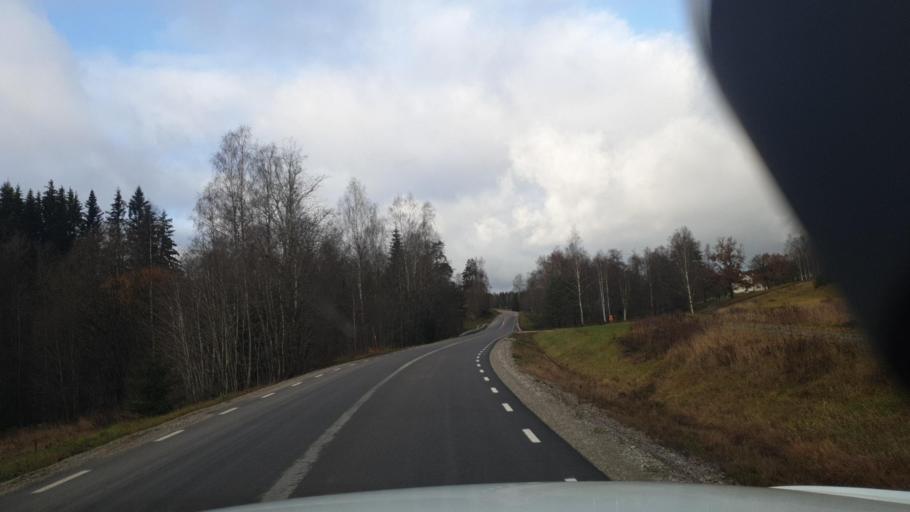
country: SE
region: Vaermland
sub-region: Sunne Kommun
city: Sunne
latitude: 59.6791
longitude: 12.8981
